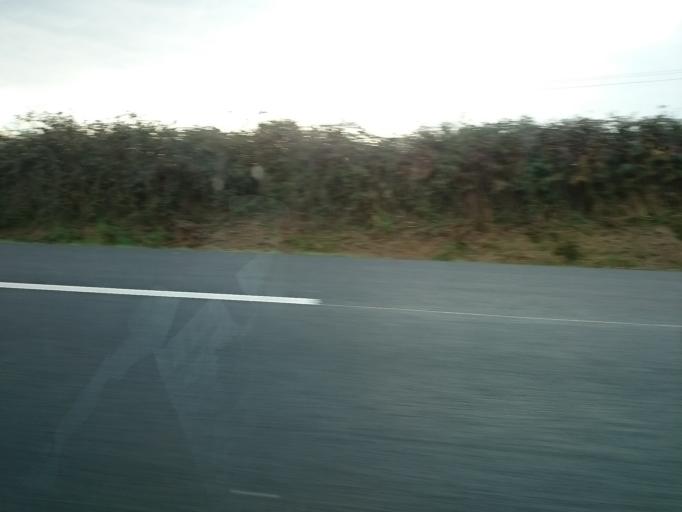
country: FR
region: Brittany
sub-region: Departement d'Ille-et-Vilaine
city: Pleumeleuc
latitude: 48.1718
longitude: -1.9142
